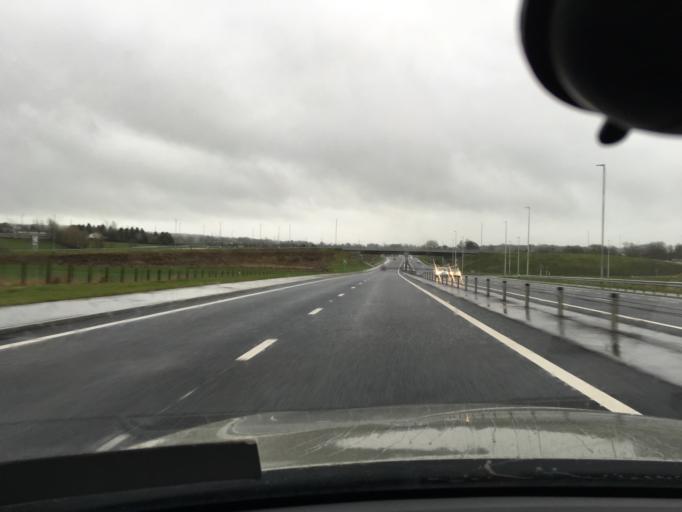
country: GB
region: Northern Ireland
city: Ballyclare
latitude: 54.7543
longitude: -5.9598
